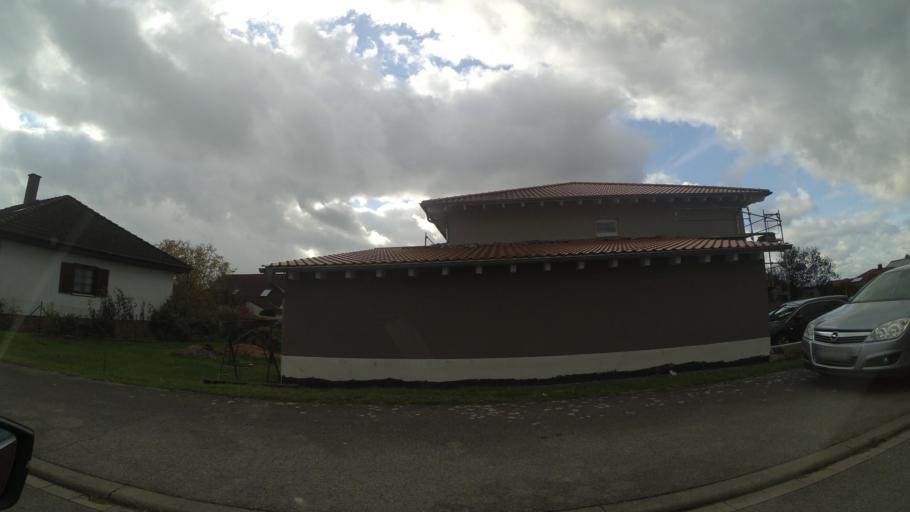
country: DE
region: Rheinland-Pfalz
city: Bottenbach
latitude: 49.1786
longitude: 7.4995
